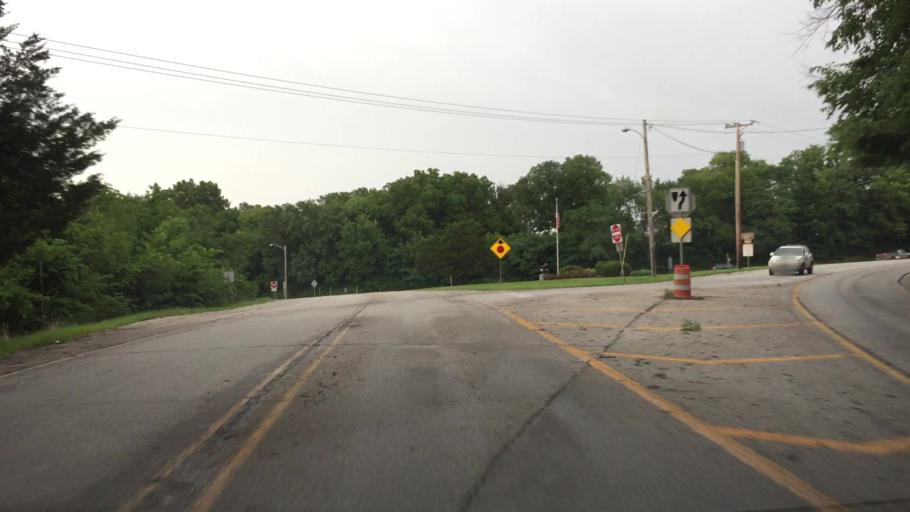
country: US
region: Illinois
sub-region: Hancock County
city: Hamilton
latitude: 40.3965
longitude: -91.3527
